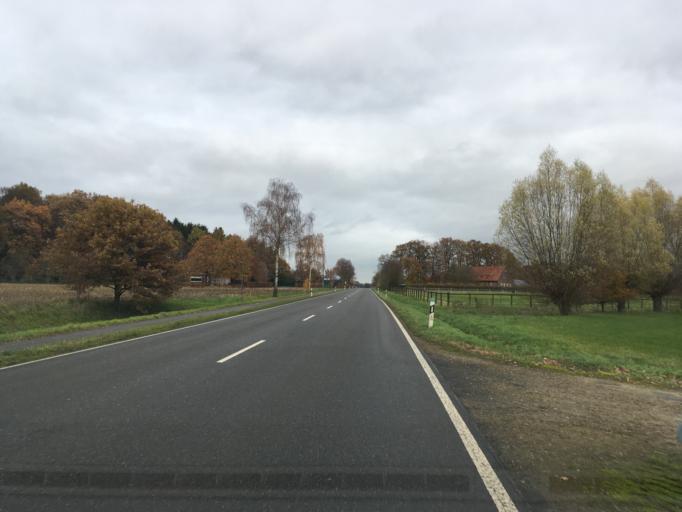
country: DE
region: North Rhine-Westphalia
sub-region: Regierungsbezirk Munster
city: Gescher
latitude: 51.9783
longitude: 7.0241
